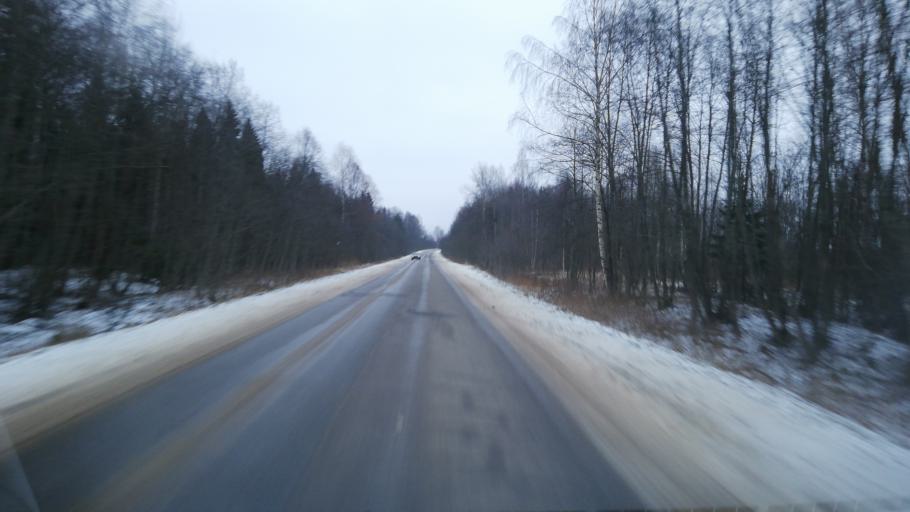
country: RU
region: Kostroma
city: Oktyabr'skiy
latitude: 57.7170
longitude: 41.1283
